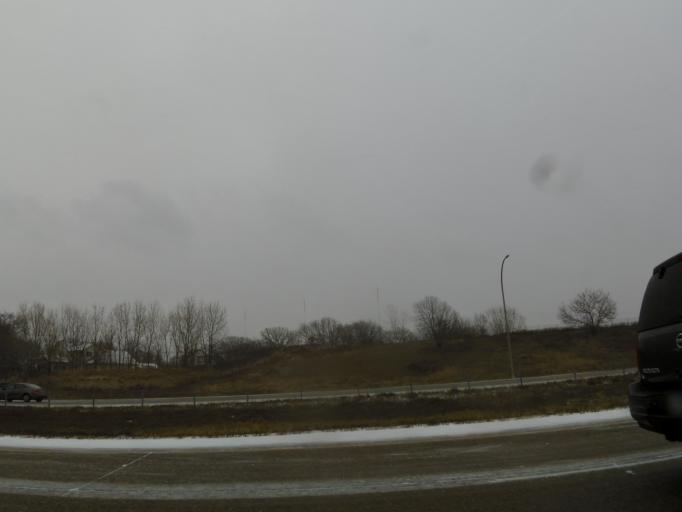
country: US
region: Minnesota
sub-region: Dakota County
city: Apple Valley
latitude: 44.7867
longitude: -93.2203
